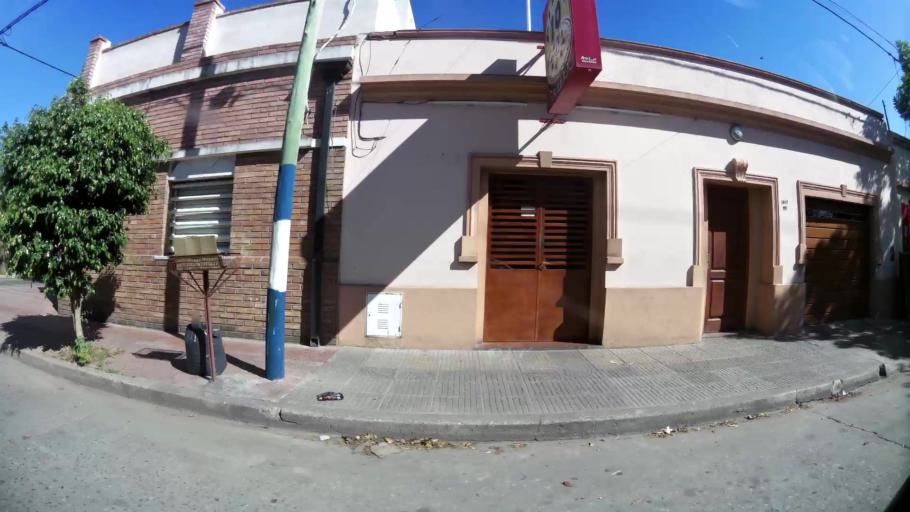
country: AR
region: Cordoba
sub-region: Departamento de Capital
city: Cordoba
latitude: -31.4397
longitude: -64.1598
